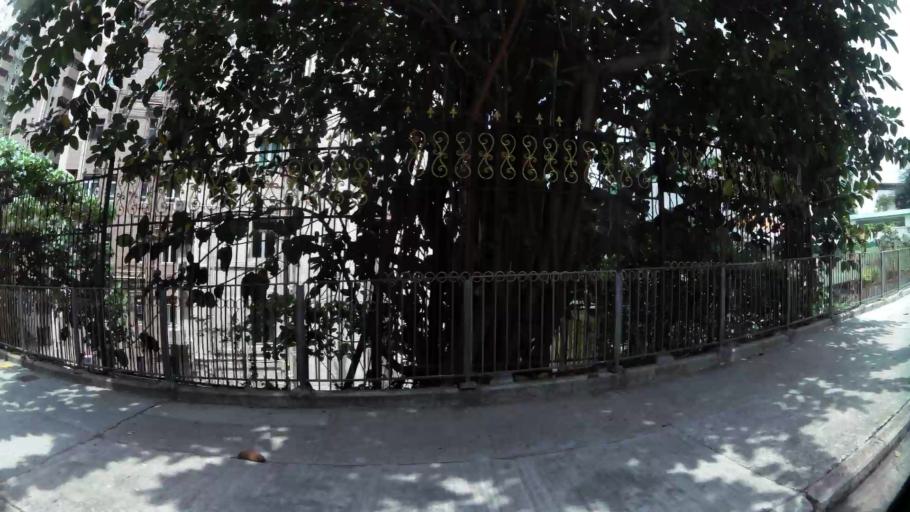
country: HK
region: Wanchai
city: Wan Chai
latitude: 22.2871
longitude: 114.1993
